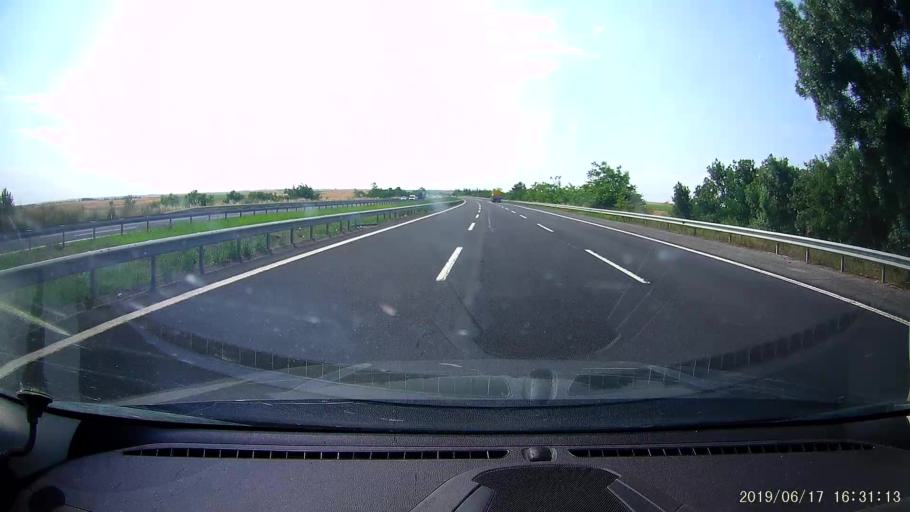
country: TR
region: Tekirdag
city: Beyazkoy
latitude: 41.3596
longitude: 27.6347
